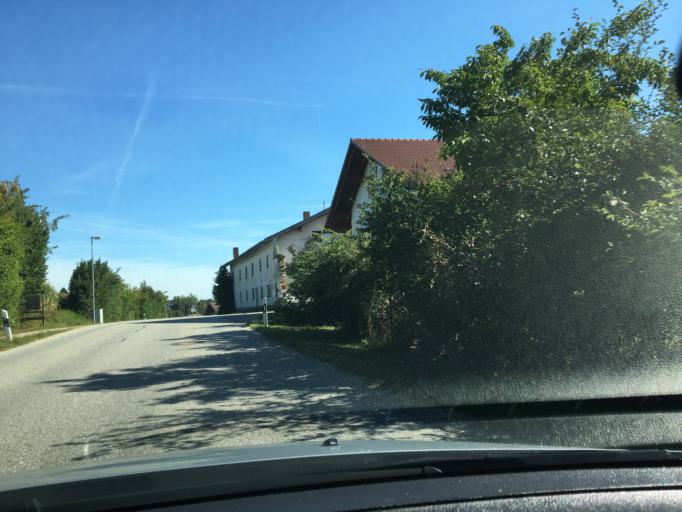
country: DE
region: Bavaria
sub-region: Lower Bavaria
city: Bodenkirchen
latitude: 48.3878
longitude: 12.3883
